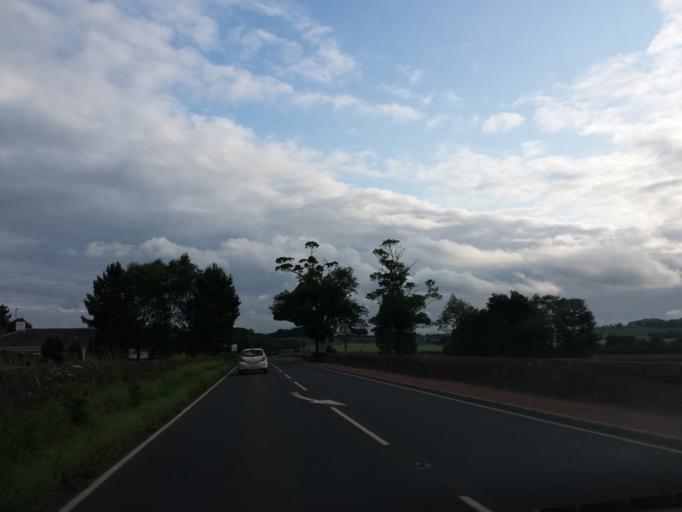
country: GB
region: Scotland
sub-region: Fife
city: Balmullo
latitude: 56.3564
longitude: -2.9219
